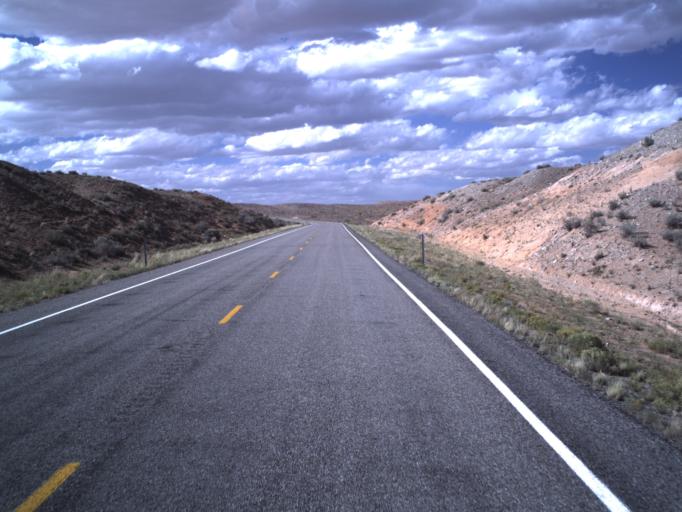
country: US
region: Utah
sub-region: Emery County
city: Ferron
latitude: 38.3278
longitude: -110.6786
